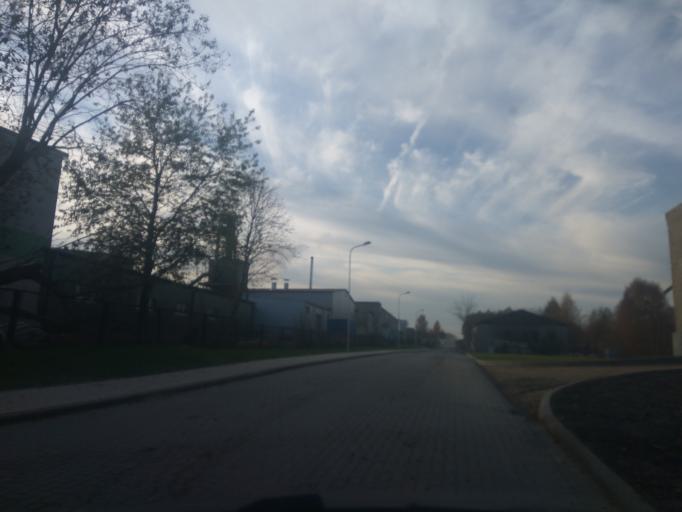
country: LV
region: Kuldigas Rajons
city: Kuldiga
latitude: 56.9821
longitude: 21.9491
